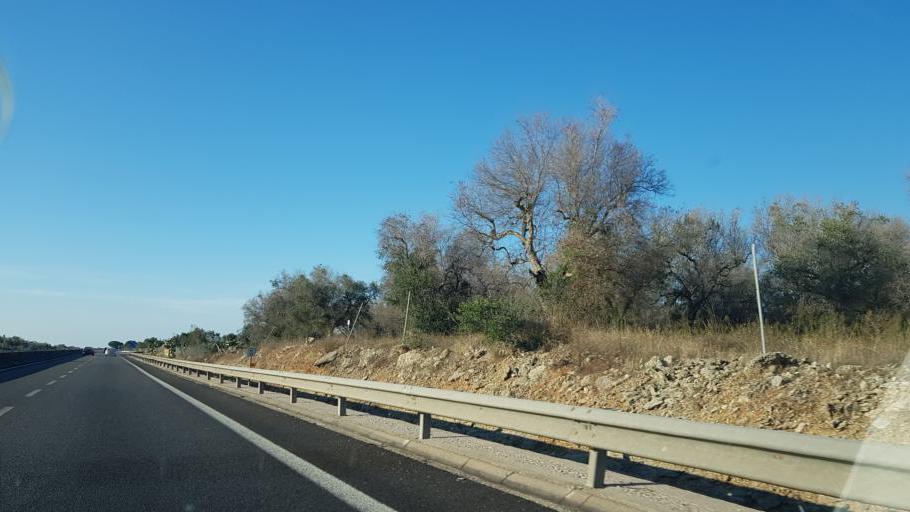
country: IT
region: Apulia
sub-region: Provincia di Lecce
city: Squinzano
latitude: 40.4462
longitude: 18.0730
